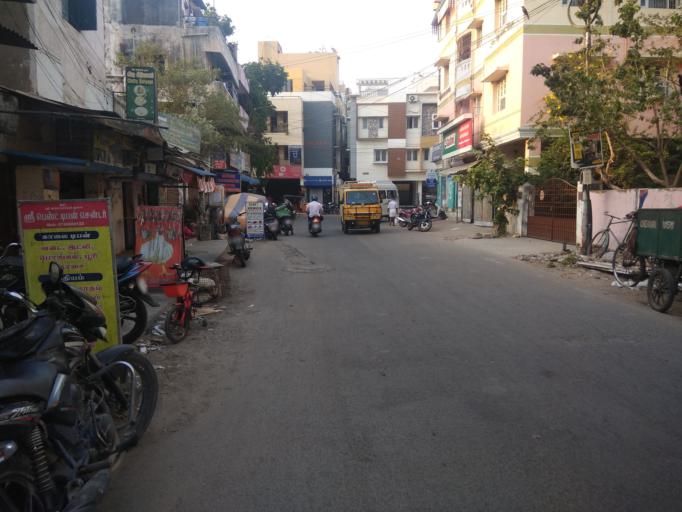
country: IN
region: Tamil Nadu
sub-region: Chennai
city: Chetput
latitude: 13.0596
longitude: 80.2226
